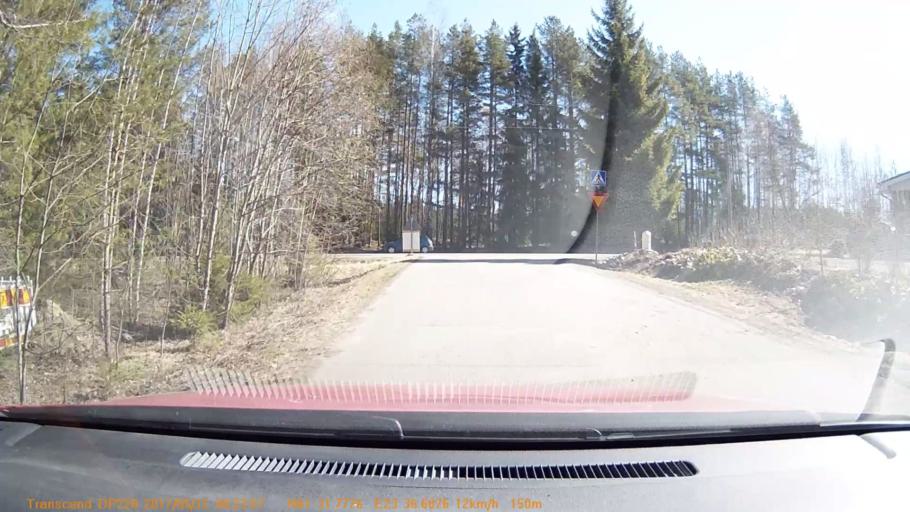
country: FI
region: Pirkanmaa
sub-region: Tampere
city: Yloejaervi
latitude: 61.5296
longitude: 23.6113
